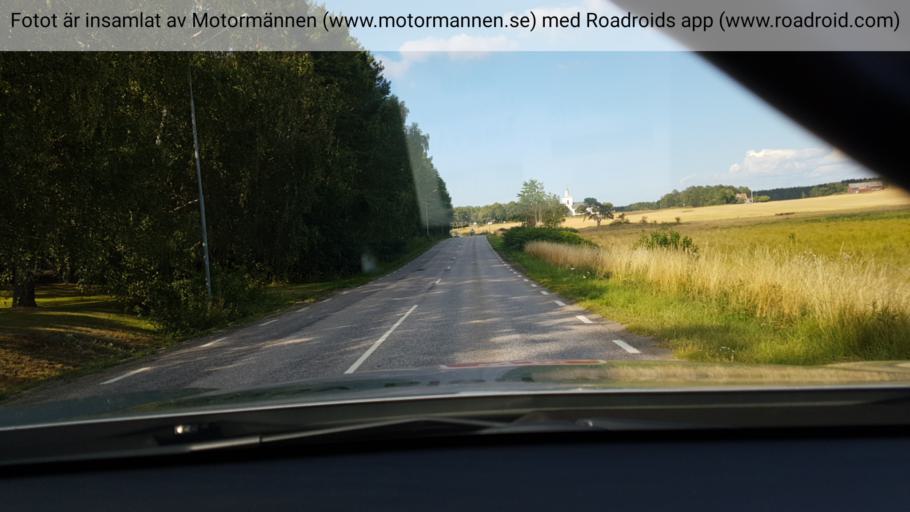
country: SE
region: Vaestra Goetaland
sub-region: Lidkopings Kommun
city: Lidkoping
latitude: 58.6490
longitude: 13.1576
